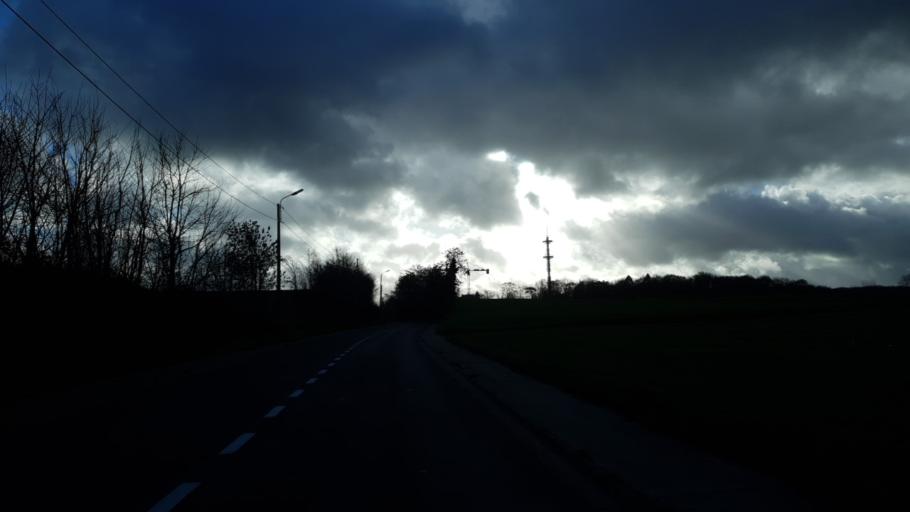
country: BE
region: Flanders
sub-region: Provincie Vlaams-Brabant
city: Kortenberg
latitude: 50.8744
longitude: 4.5781
